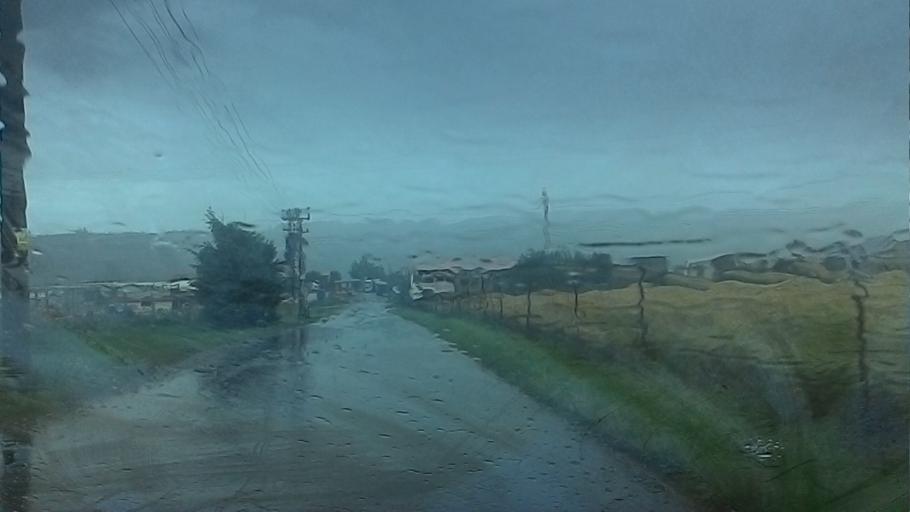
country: SK
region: Presovsky
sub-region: Okres Poprad
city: Poprad
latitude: 49.0310
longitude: 20.3448
